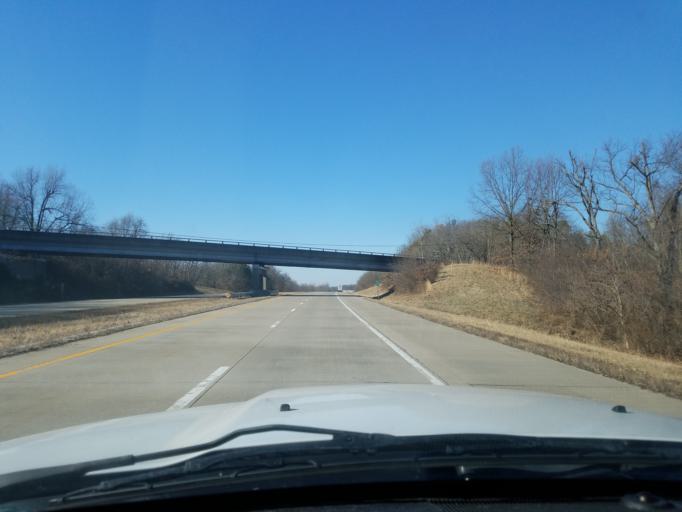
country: US
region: Indiana
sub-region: Warrick County
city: Newburgh
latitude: 37.7593
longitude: -87.4148
